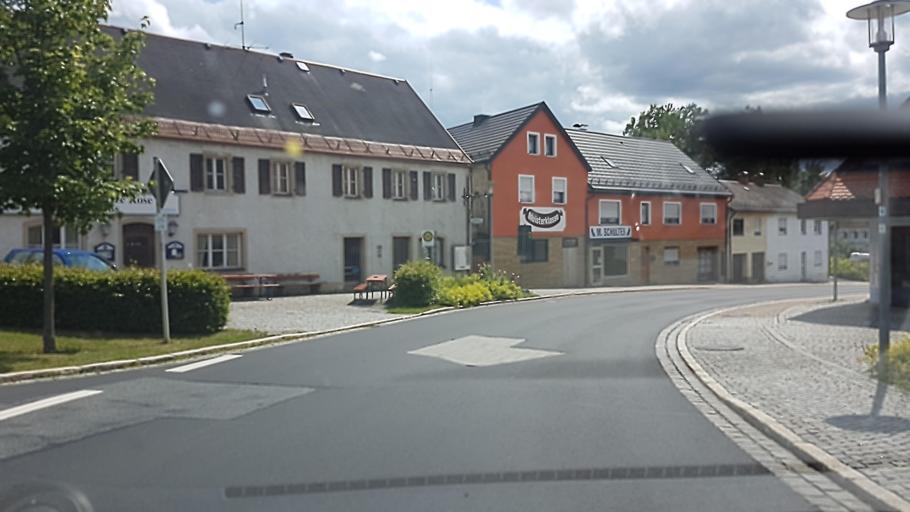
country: DE
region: Bavaria
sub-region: Upper Palatinate
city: Brand
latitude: 49.9593
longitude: 11.9084
